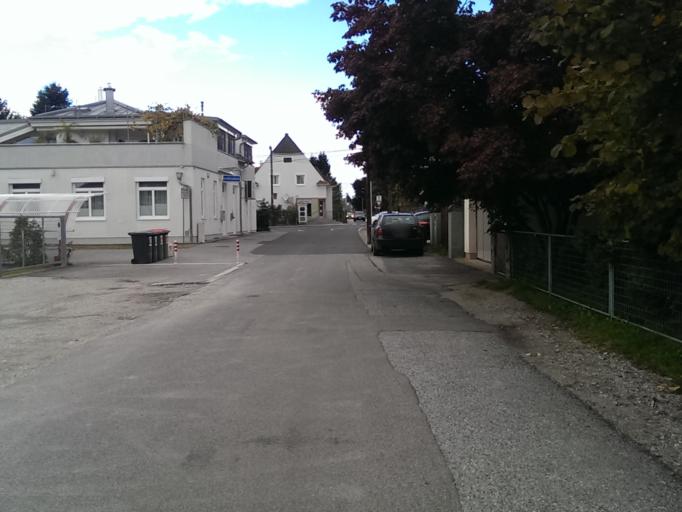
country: AT
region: Styria
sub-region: Graz Stadt
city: Graz
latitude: 47.0521
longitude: 15.4711
